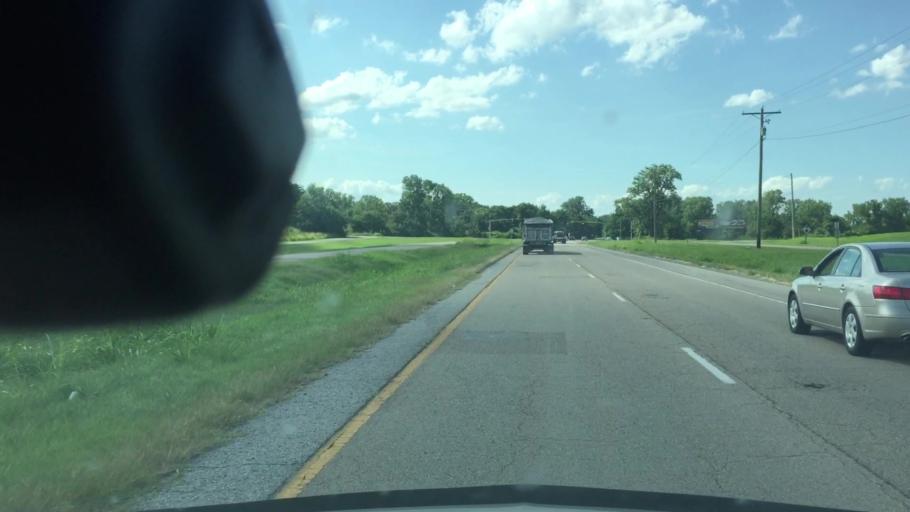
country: US
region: Illinois
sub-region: Madison County
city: Madison
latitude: 38.6622
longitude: -90.1401
